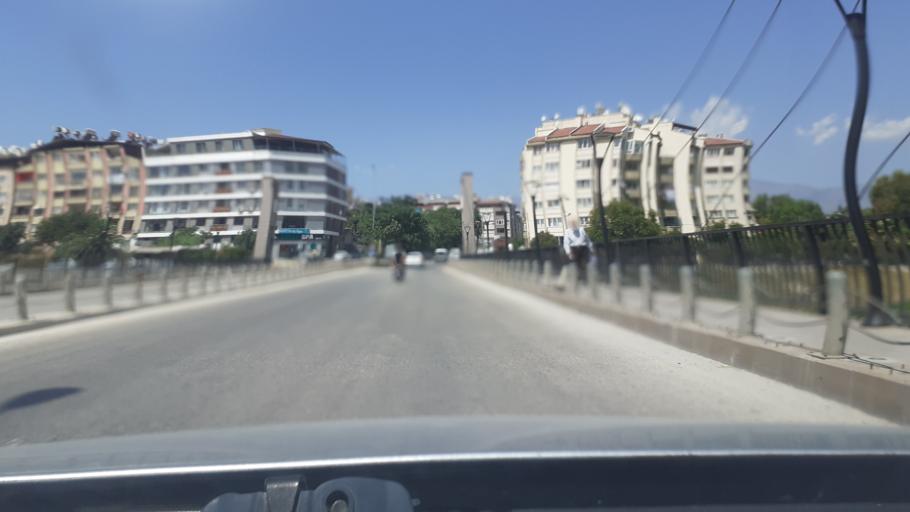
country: TR
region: Hatay
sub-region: Antakya Ilcesi
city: Antakya
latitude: 36.1951
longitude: 36.1569
